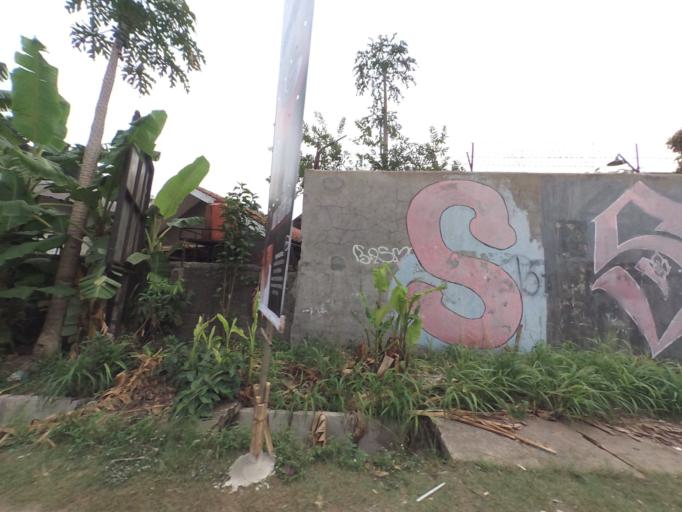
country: ID
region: West Java
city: Sidoger Lebak
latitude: -6.5664
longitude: 106.5986
